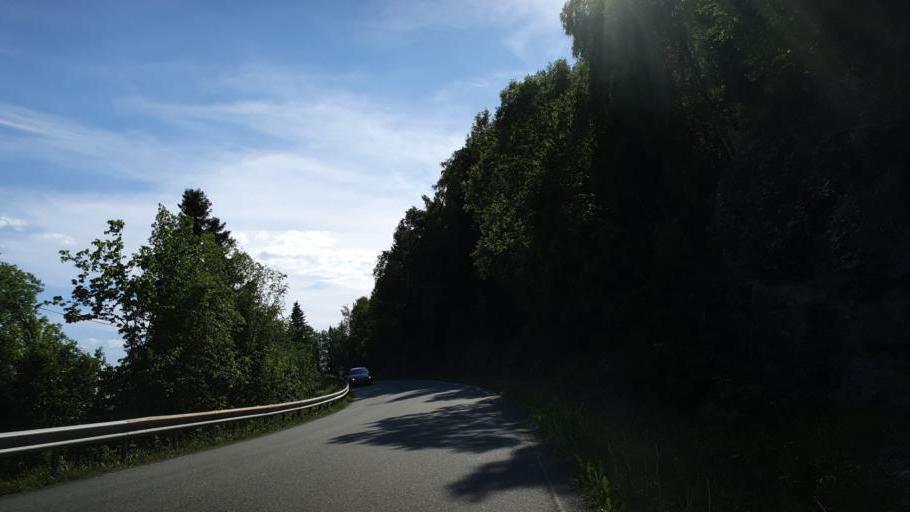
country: NO
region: Nord-Trondelag
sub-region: Leksvik
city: Leksvik
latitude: 63.6378
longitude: 10.5816
